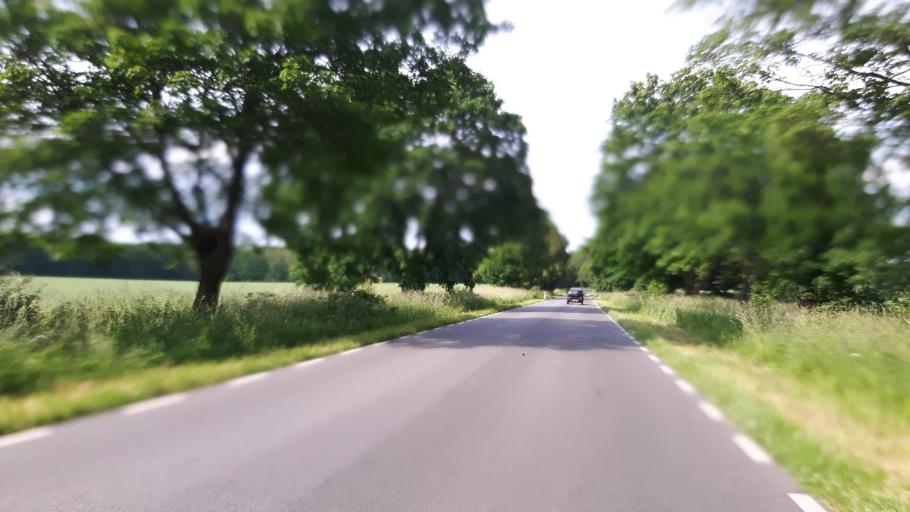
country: PL
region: West Pomeranian Voivodeship
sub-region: Powiat goleniowski
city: Nowogard
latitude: 53.7190
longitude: 15.1208
